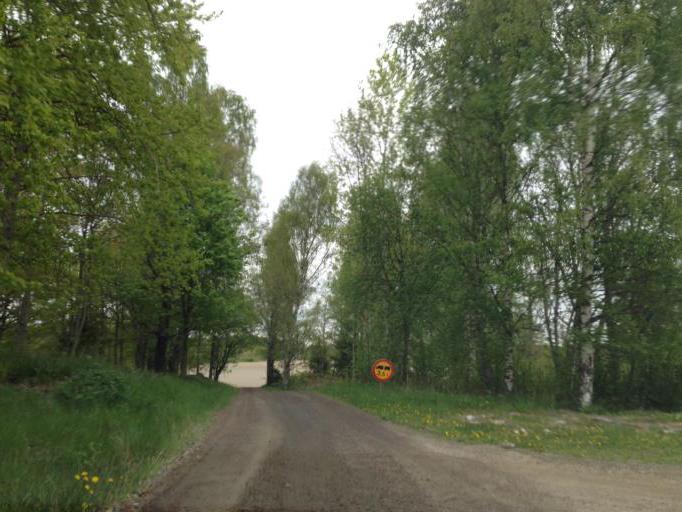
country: SE
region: Soedermanland
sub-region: Eskilstuna Kommun
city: Kvicksund
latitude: 59.4376
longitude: 16.3004
